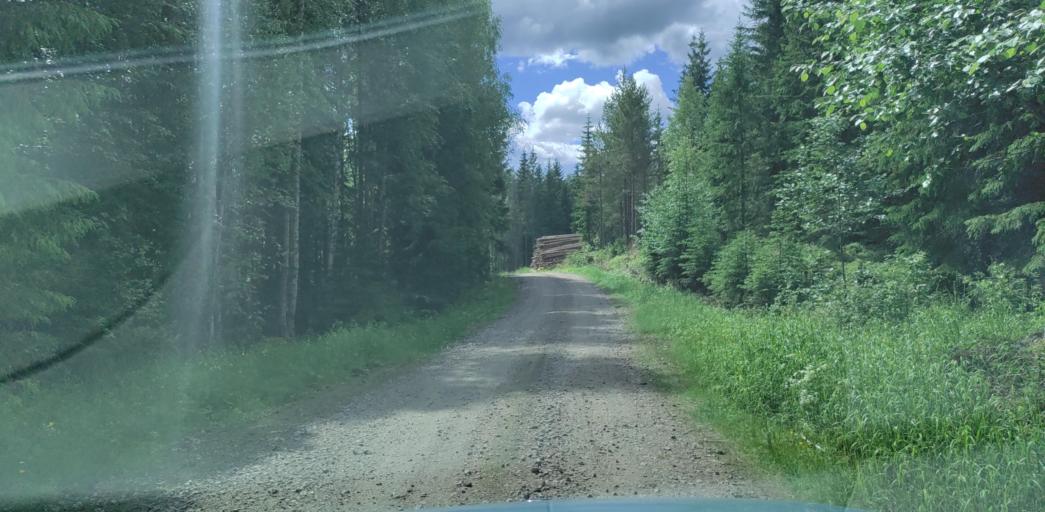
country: SE
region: Vaermland
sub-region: Hagfors Kommun
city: Ekshaerad
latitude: 60.1078
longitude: 13.3238
